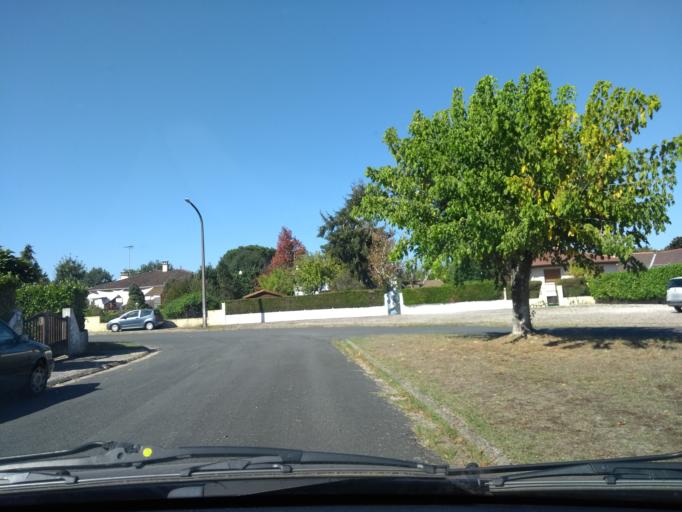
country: FR
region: Aquitaine
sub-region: Departement de la Gironde
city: Salles
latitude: 44.5503
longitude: -0.8613
